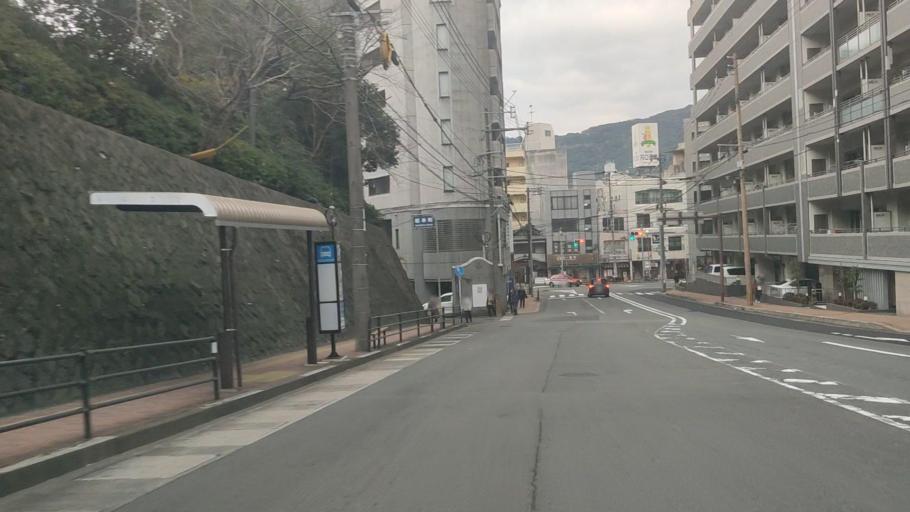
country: JP
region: Nagasaki
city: Nagasaki-shi
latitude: 32.7700
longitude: 129.8672
